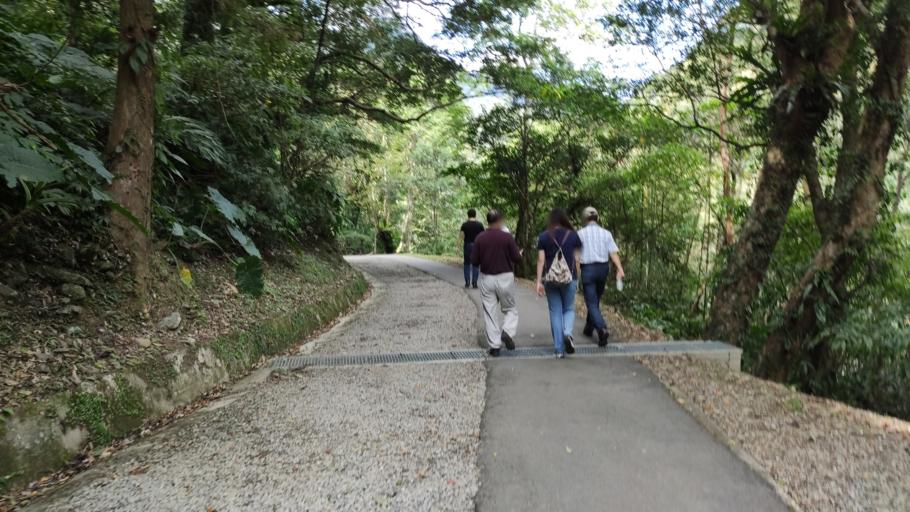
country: TW
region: Taiwan
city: Daxi
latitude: 24.8282
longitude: 121.4460
